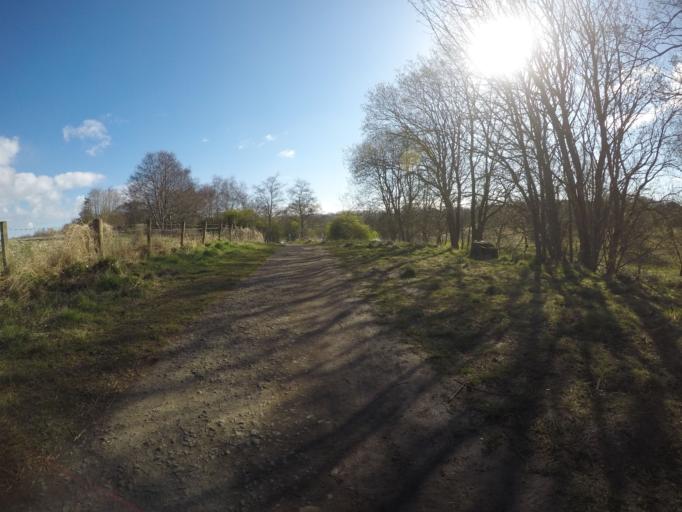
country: GB
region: Scotland
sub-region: North Ayrshire
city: Irvine
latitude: 55.6444
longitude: -4.6635
